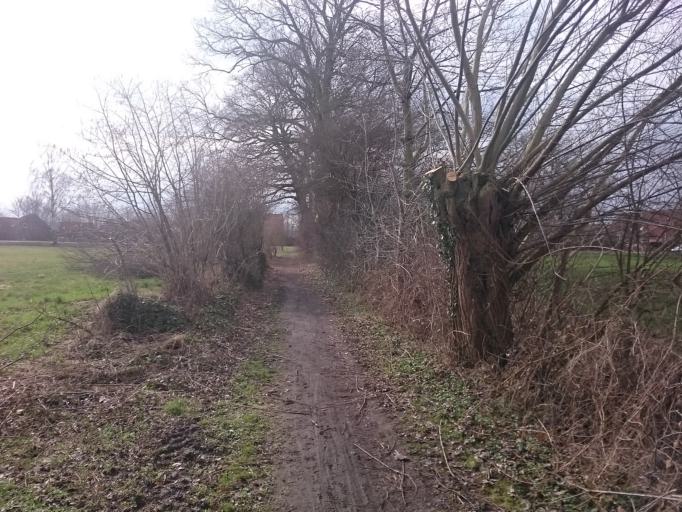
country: DE
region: Lower Saxony
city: Lauenhagen
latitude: 52.3573
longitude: 9.2026
